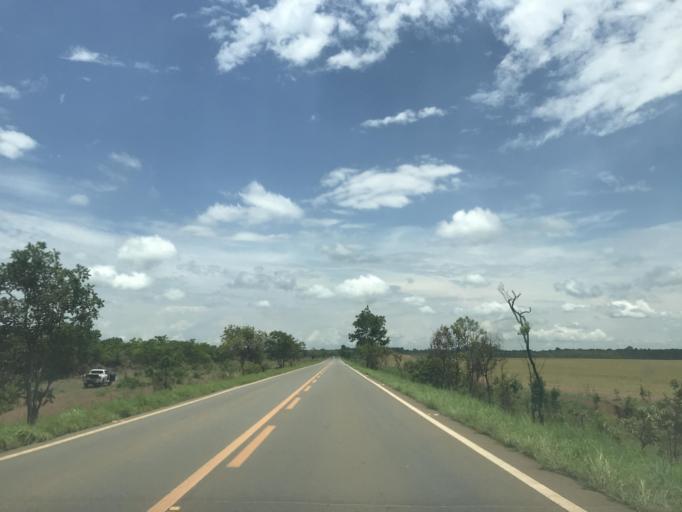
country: BR
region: Goias
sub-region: Luziania
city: Luziania
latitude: -16.3986
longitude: -48.1323
